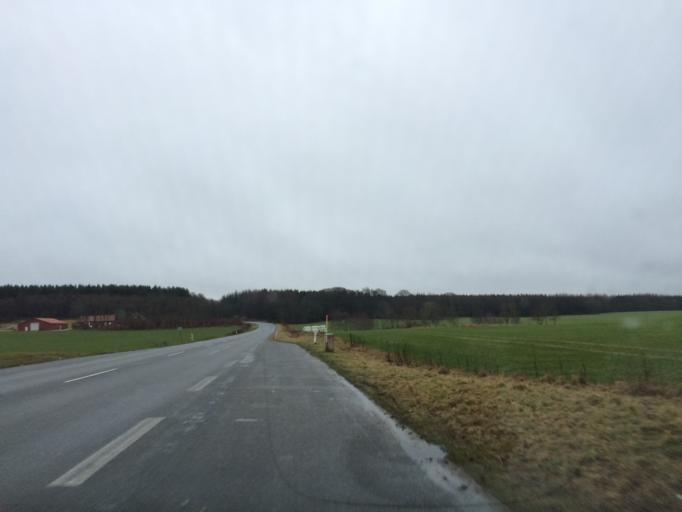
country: DK
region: North Denmark
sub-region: Mariagerfjord Kommune
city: Arden
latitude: 56.8067
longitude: 9.8177
